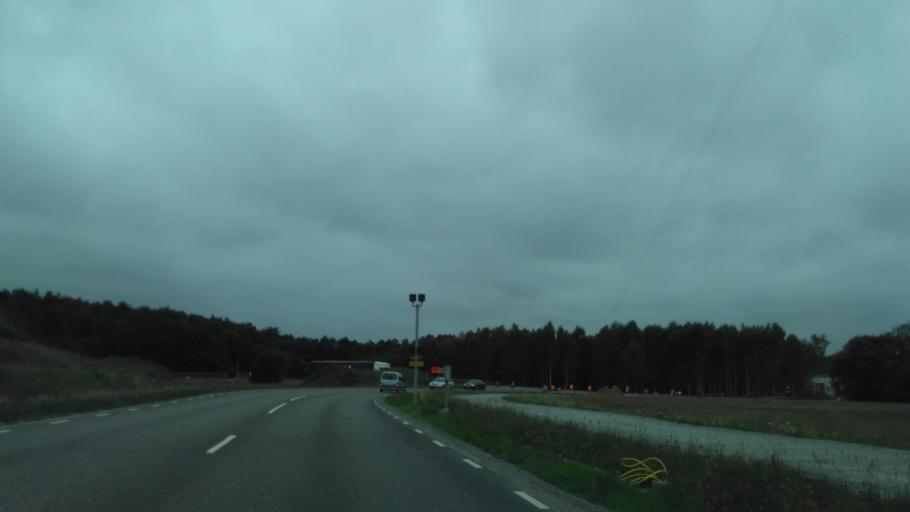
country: SE
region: Vaestra Goetaland
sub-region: Alingsas Kommun
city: Alingsas
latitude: 57.9374
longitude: 12.5792
